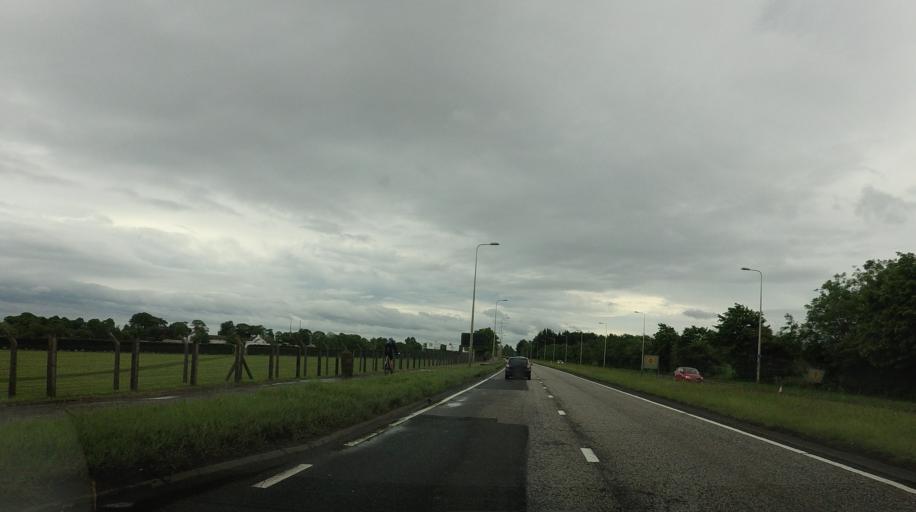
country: GB
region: Scotland
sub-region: Edinburgh
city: Ratho
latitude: 55.9386
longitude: -3.3832
